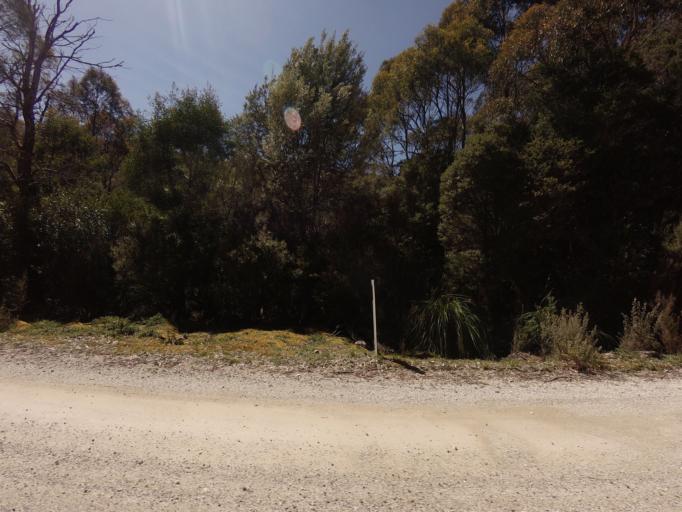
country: AU
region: Tasmania
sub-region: Huon Valley
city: Geeveston
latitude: -43.0112
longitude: 146.3637
